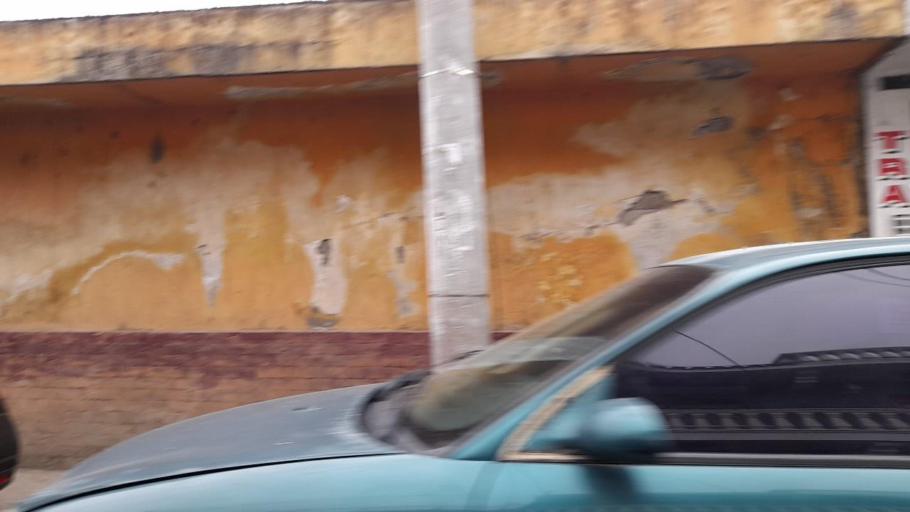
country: GT
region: Quetzaltenango
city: Quetzaltenango
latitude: 14.8339
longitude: -91.5105
